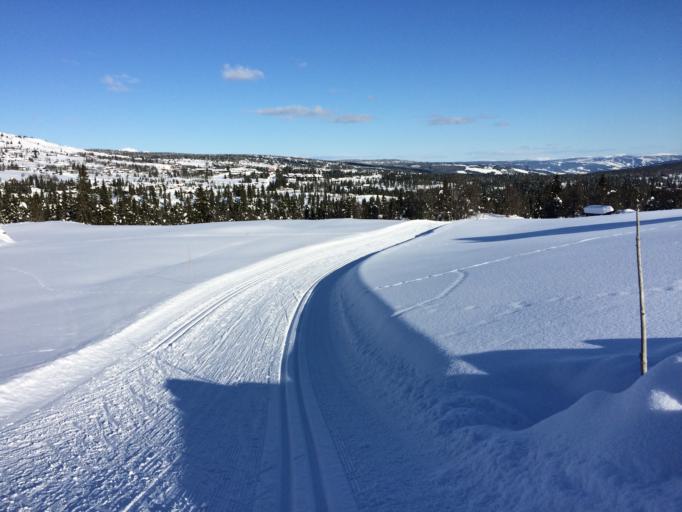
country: NO
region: Oppland
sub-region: Gausdal
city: Segalstad bru
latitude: 61.3351
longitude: 10.0532
